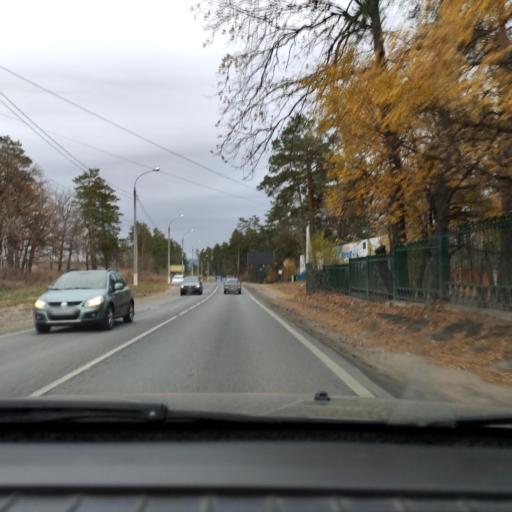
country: RU
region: Samara
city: Tol'yatti
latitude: 53.4852
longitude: 49.3152
